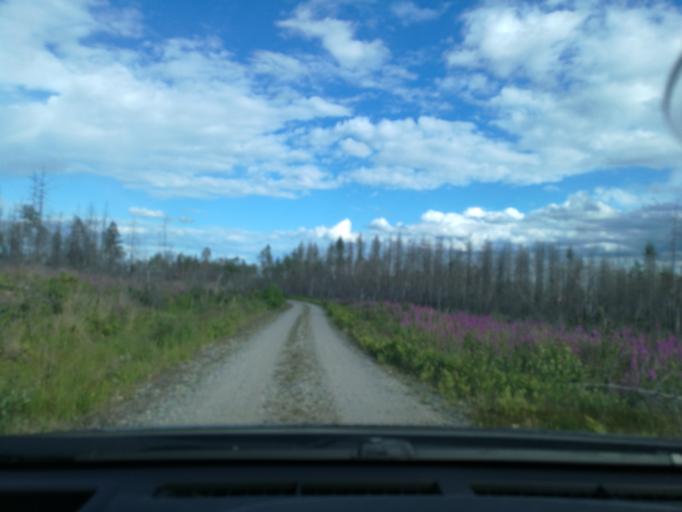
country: SE
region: Vaestmanland
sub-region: Surahammars Kommun
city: Ramnas
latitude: 59.8507
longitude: 16.2638
